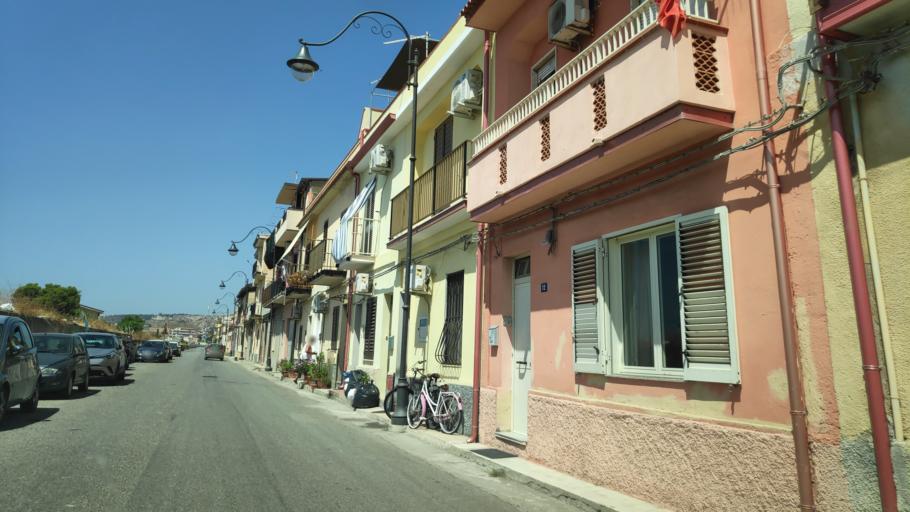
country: IT
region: Calabria
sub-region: Provincia di Reggio Calabria
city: Bova Marina
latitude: 37.9294
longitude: 15.9304
